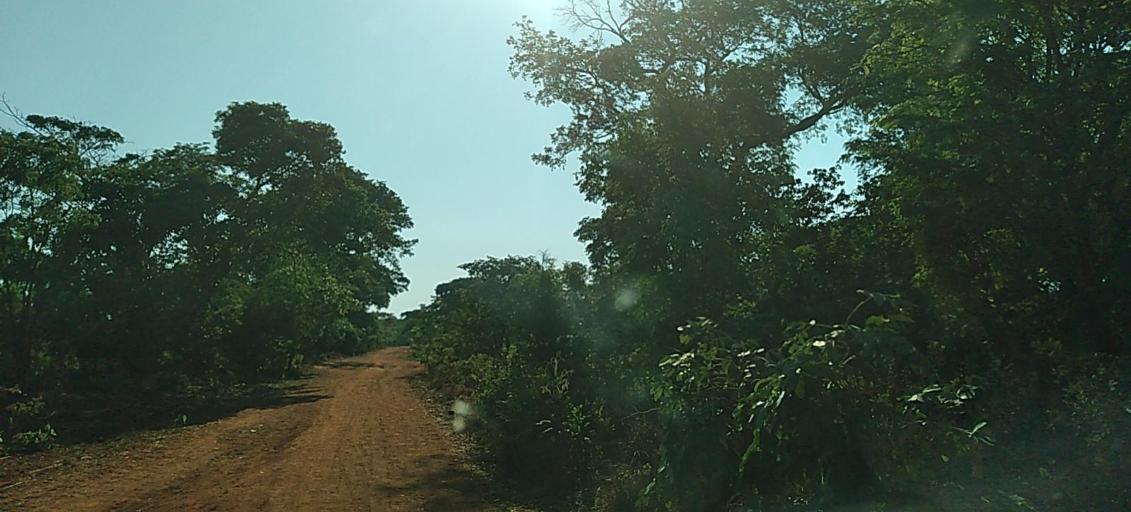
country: ZM
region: Copperbelt
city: Luanshya
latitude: -13.4592
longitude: 28.8168
